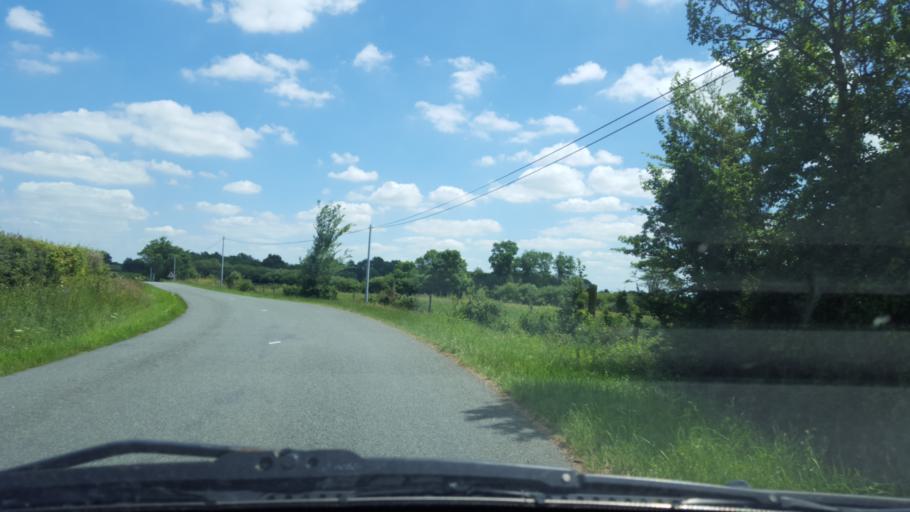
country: FR
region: Pays de la Loire
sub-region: Departement de la Vendee
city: Saint-Philbert-de-Bouaine
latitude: 46.9899
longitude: -1.5367
